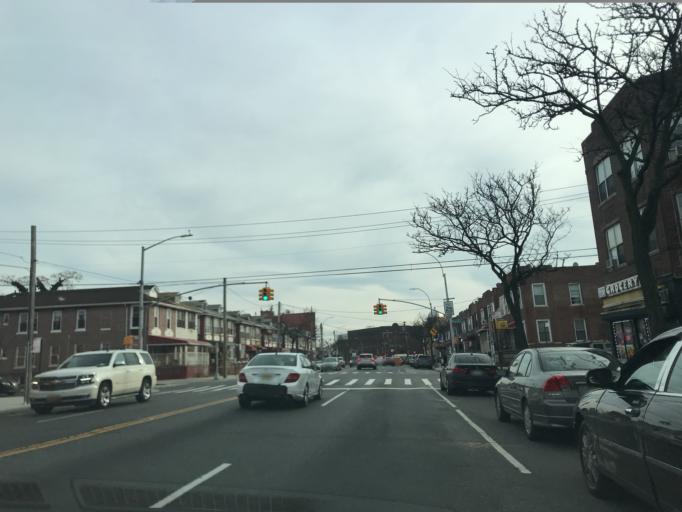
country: US
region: New York
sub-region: Kings County
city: East New York
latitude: 40.6637
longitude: -73.8937
